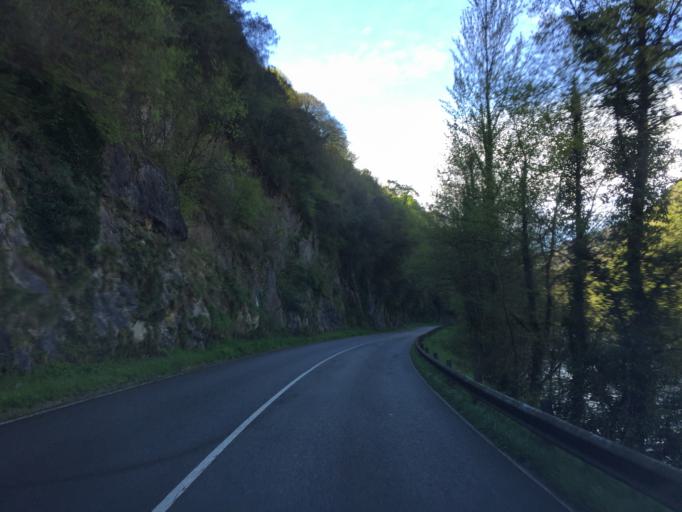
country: ES
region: Asturias
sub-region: Province of Asturias
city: Proaza
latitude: 43.2859
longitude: -5.9840
